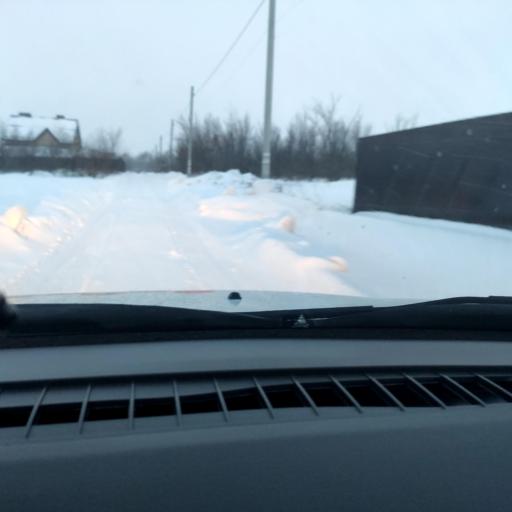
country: RU
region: Samara
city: Dubovyy Umet
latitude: 53.0296
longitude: 50.2301
